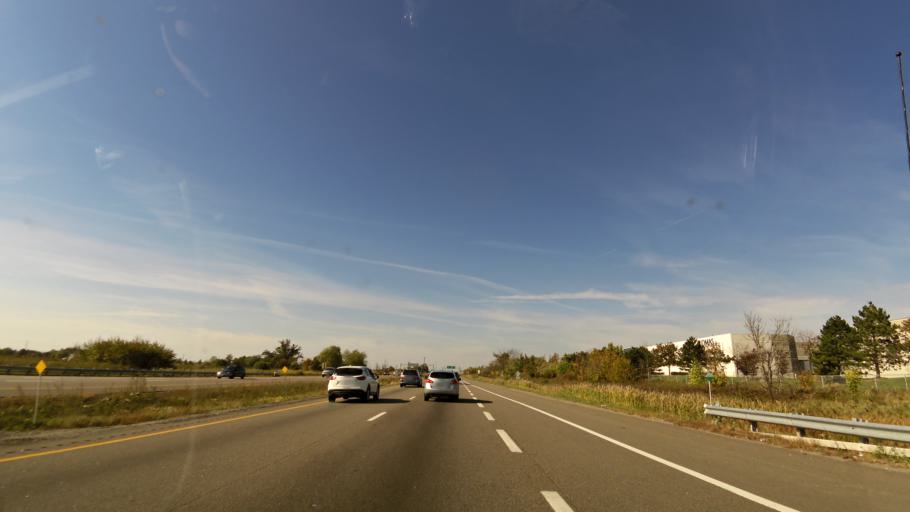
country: CA
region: Ontario
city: Oakville
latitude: 43.5156
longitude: -79.6995
